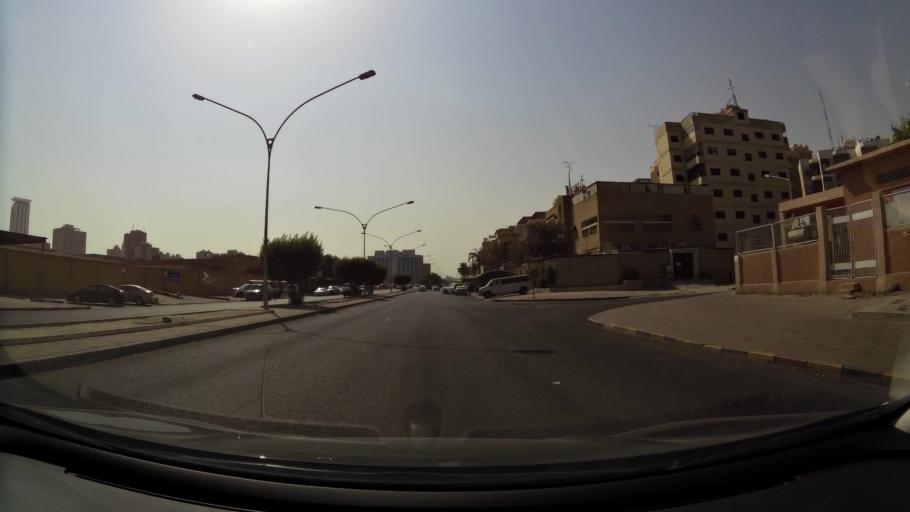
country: KW
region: Al Ahmadi
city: Al Fahahil
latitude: 29.0822
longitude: 48.1322
